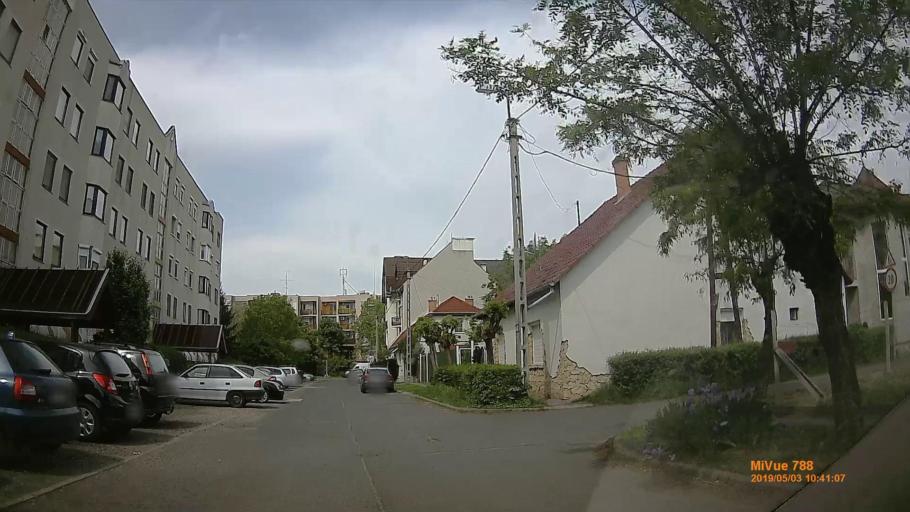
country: HU
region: Jasz-Nagykun-Szolnok
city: Szolnok
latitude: 47.1833
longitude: 20.1937
